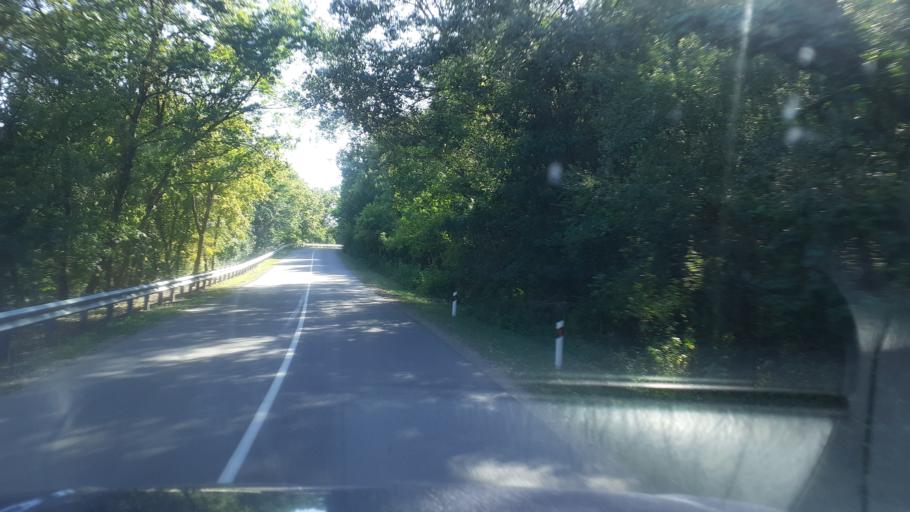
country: RU
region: Krasnodarskiy
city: Azovskaya
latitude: 44.7520
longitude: 38.5552
